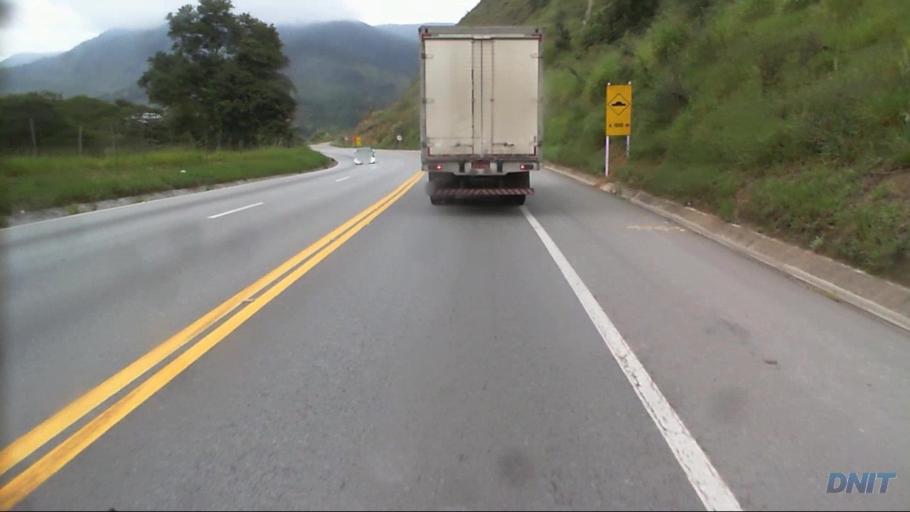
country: BR
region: Minas Gerais
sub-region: Nova Era
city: Nova Era
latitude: -19.6519
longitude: -42.9484
